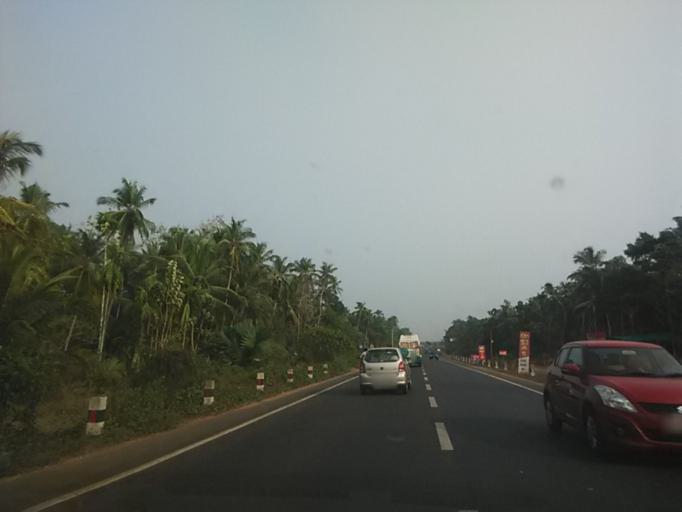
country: IN
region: Kerala
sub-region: Kozhikode
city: Kozhikode
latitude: 11.3064
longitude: 75.7877
